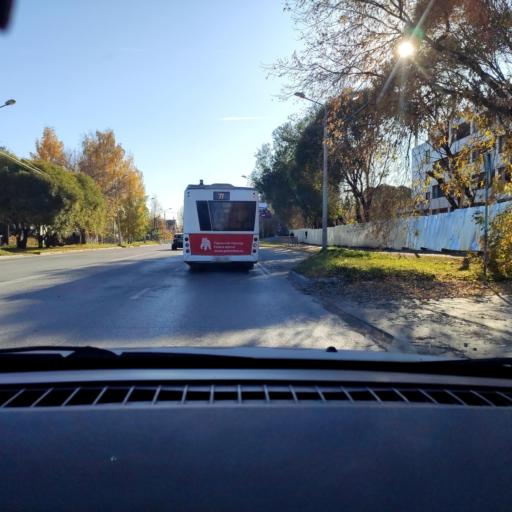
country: RU
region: Perm
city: Perm
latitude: 58.0630
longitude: 56.3627
